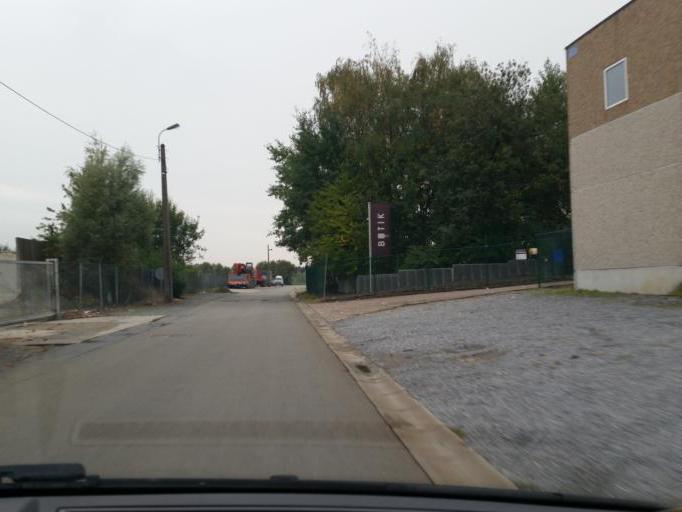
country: BE
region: Flanders
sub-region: Provincie Antwerpen
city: Hemiksem
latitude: 51.1577
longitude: 4.3382
